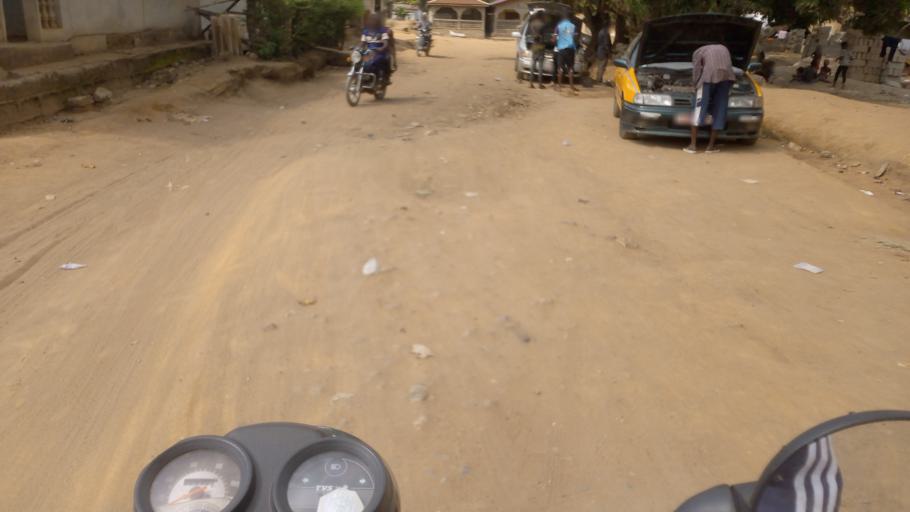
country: SL
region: Western Area
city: Waterloo
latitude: 8.3278
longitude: -13.0615
